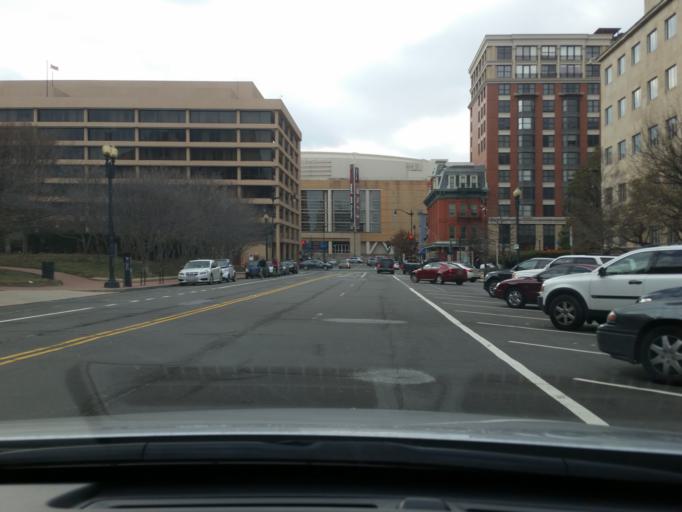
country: US
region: Washington, D.C.
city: Washington, D.C.
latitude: 38.8983
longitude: -77.0177
